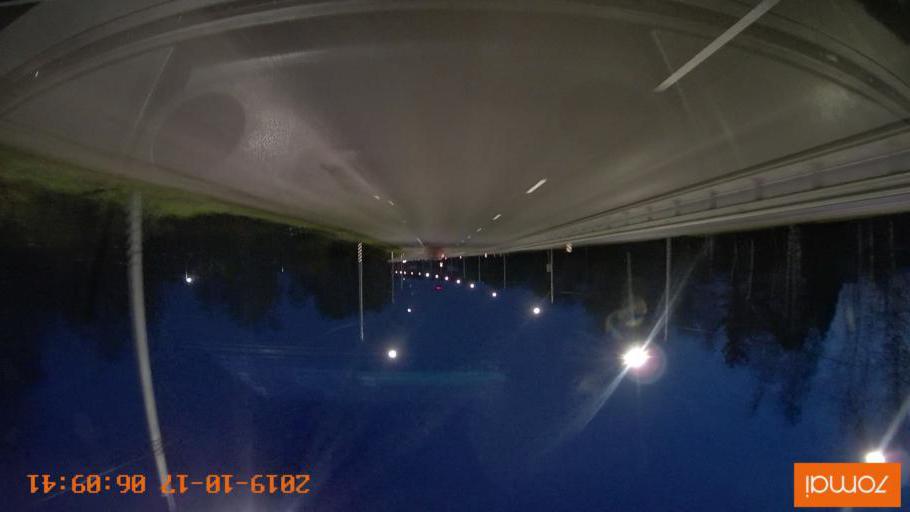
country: RU
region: Ivanovo
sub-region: Gorod Ivanovo
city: Ivanovo
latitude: 56.9384
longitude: 40.9720
